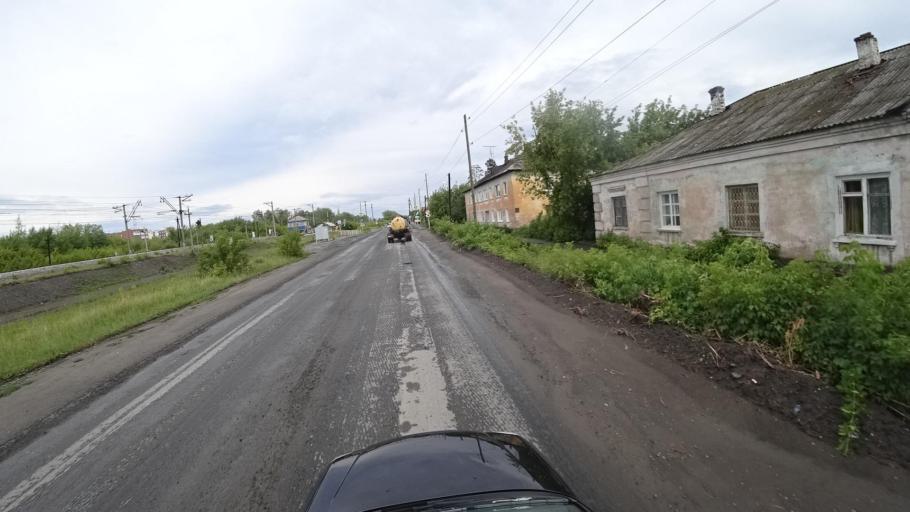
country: RU
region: Sverdlovsk
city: Kamyshlov
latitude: 56.8428
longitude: 62.7427
